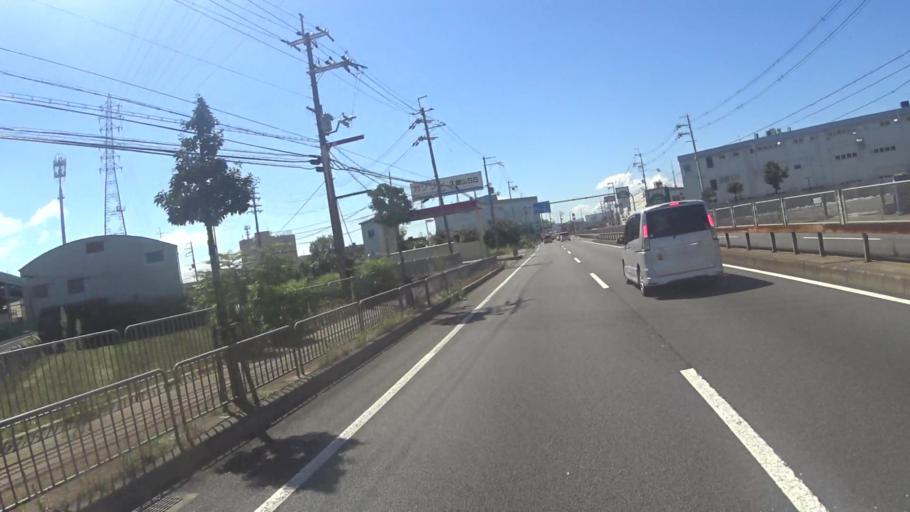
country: JP
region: Kyoto
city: Yawata
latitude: 34.8929
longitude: 135.7440
